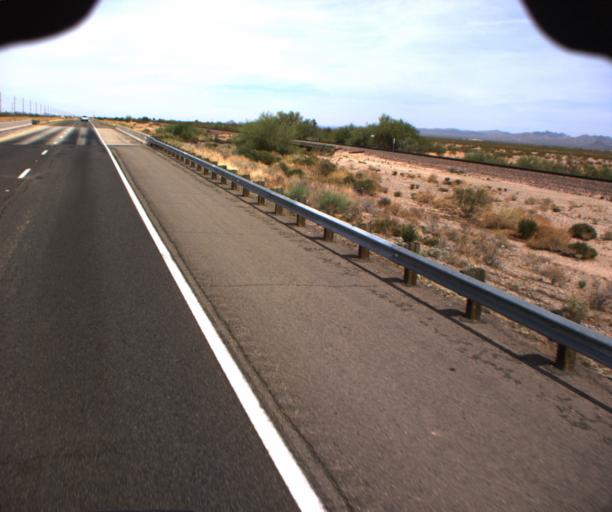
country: US
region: Arizona
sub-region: Maricopa County
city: Sun City West
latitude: 33.7473
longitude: -112.4892
